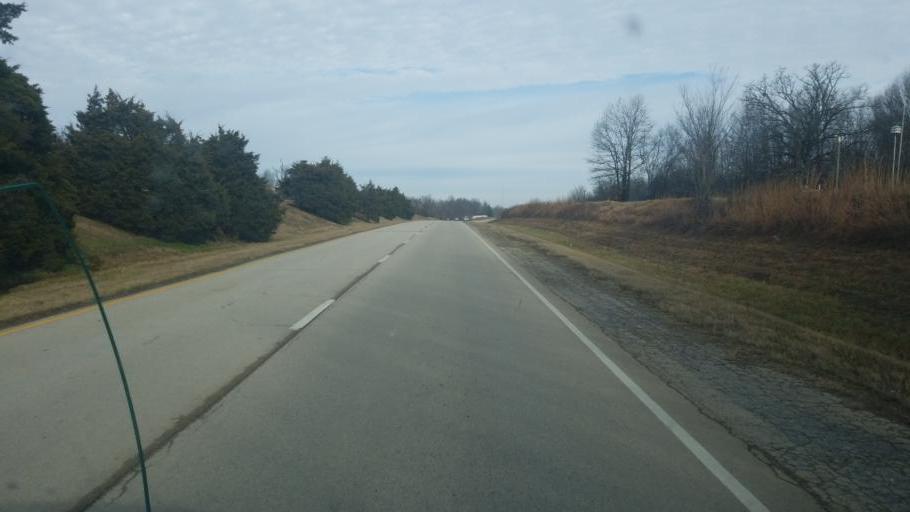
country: US
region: Missouri
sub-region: Stoddard County
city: Dexter
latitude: 36.8370
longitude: -89.9417
